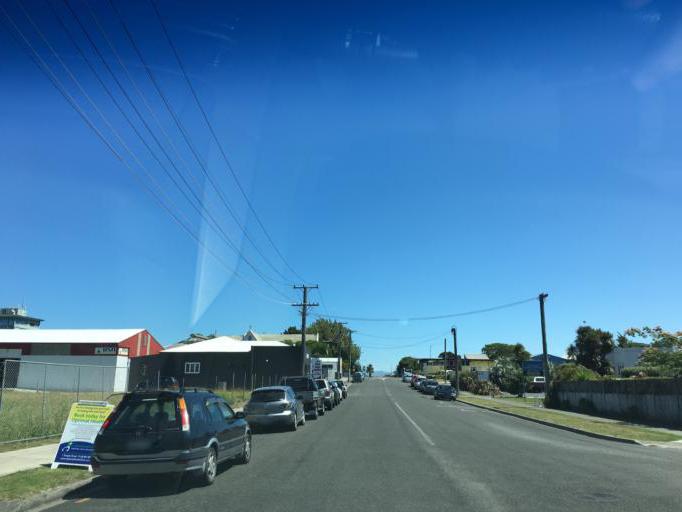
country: NZ
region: Gisborne
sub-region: Gisborne District
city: Gisborne
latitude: -38.6619
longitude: 178.0254
